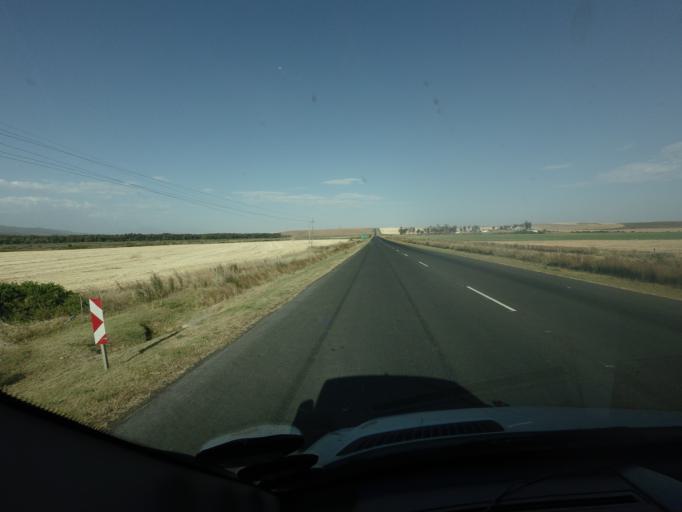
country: ZA
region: Western Cape
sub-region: Cape Winelands District Municipality
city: Ashton
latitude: -34.1549
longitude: 19.9337
